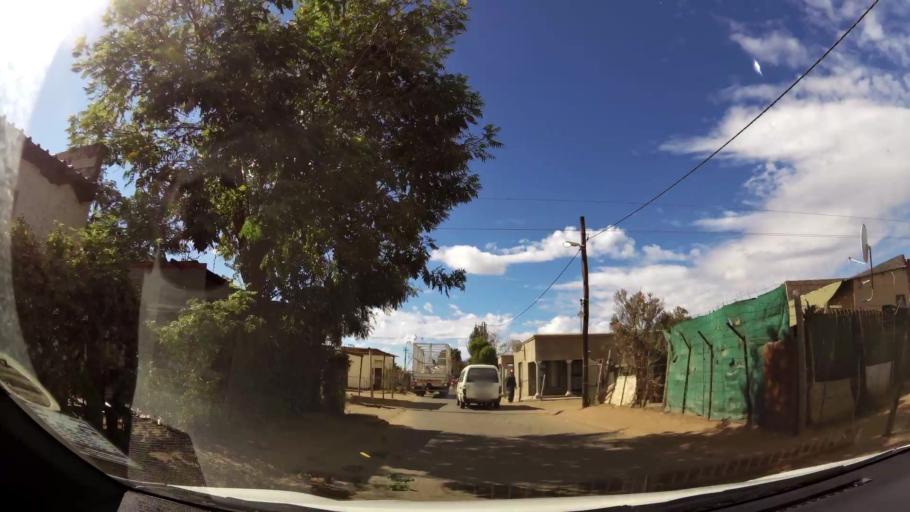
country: ZA
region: Limpopo
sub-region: Waterberg District Municipality
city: Bela-Bela
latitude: -24.8857
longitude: 28.3245
